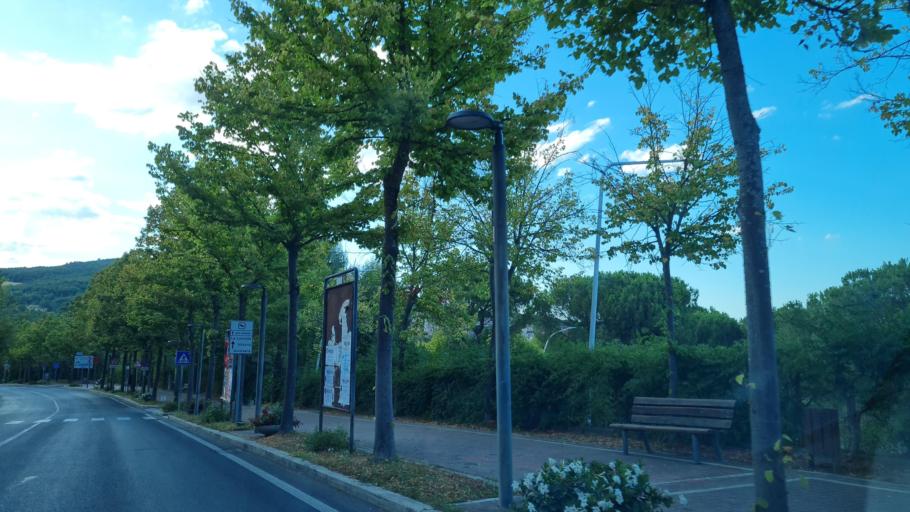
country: IT
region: Tuscany
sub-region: Provincia di Siena
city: Chianciano Terme
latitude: 43.0382
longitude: 11.8208
